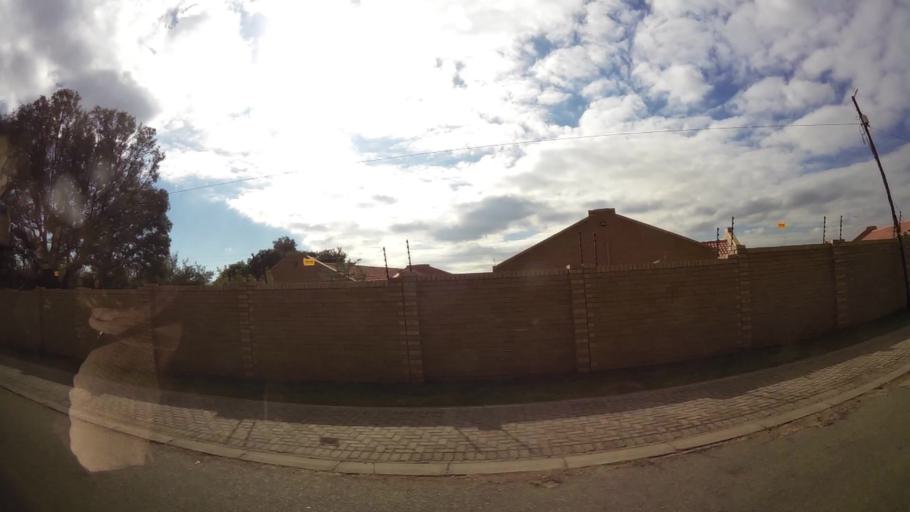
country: ZA
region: Gauteng
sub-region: City of Johannesburg Metropolitan Municipality
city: Roodepoort
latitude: -26.1025
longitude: 27.8719
